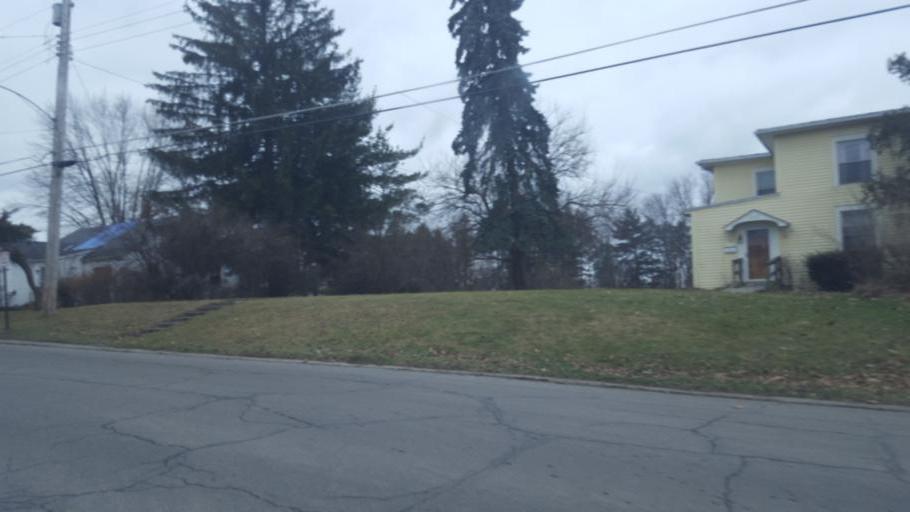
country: US
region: Ohio
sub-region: Morrow County
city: Mount Gilead
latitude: 40.5549
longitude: -82.8354
